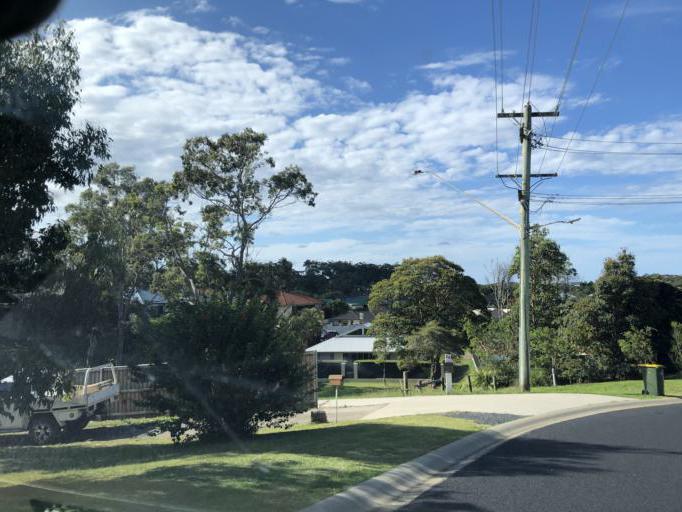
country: AU
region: New South Wales
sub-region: Coffs Harbour
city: Moonee Beach
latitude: -30.2330
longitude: 153.1490
